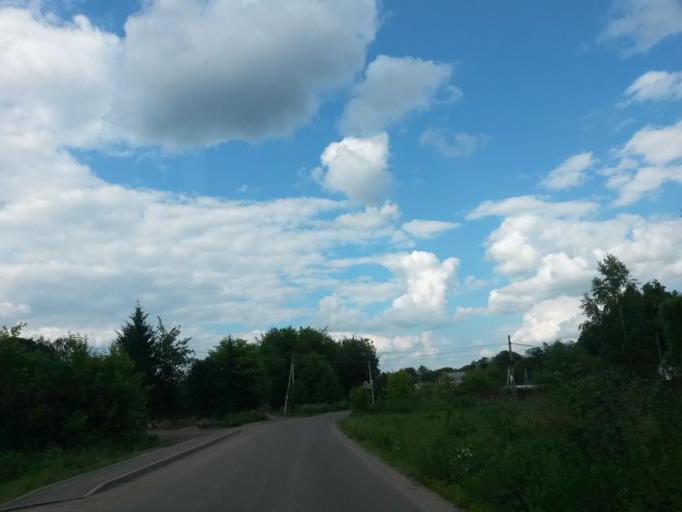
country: RU
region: Moskovskaya
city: Lyubuchany
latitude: 55.2490
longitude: 37.5471
